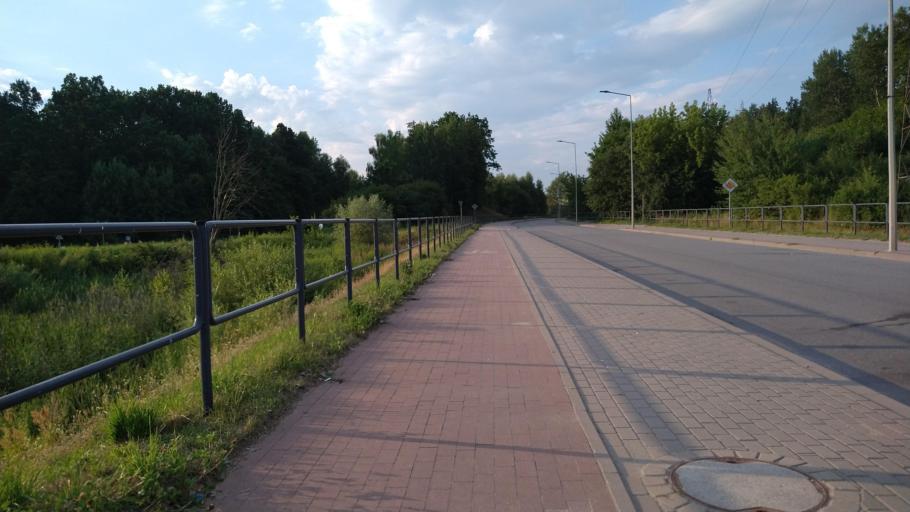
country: PL
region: Warmian-Masurian Voivodeship
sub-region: Powiat olsztynski
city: Olsztyn
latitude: 53.7838
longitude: 20.5513
